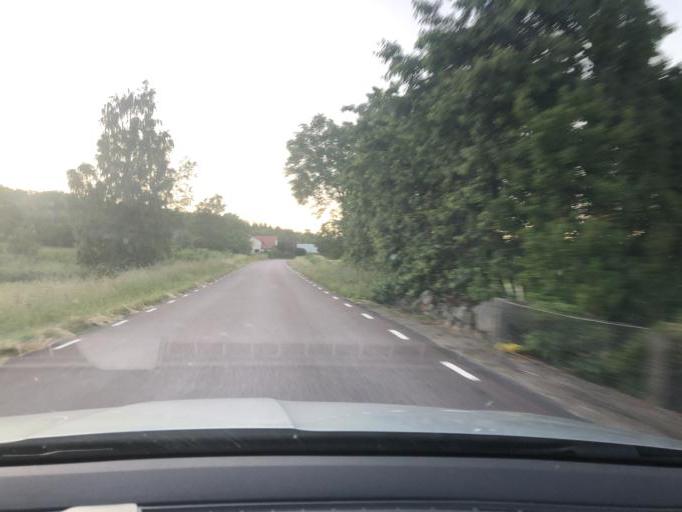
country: SE
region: Blekinge
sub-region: Solvesborgs Kommun
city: Soelvesborg
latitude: 56.1326
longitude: 14.6074
